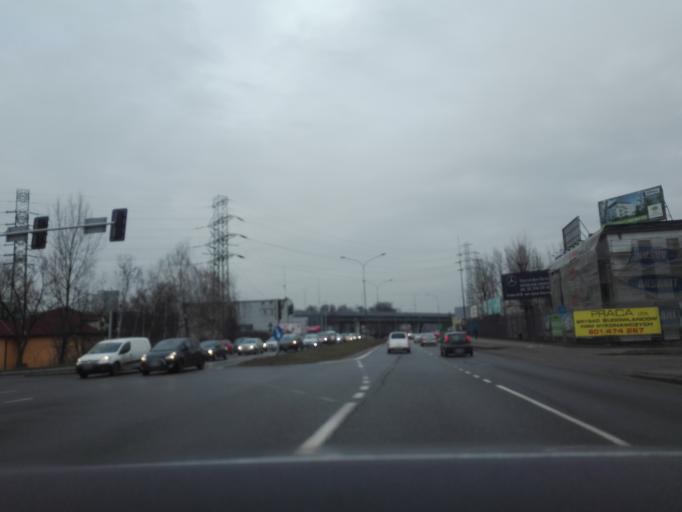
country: PL
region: Silesian Voivodeship
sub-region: Katowice
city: Katowice
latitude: 50.2680
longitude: 18.9901
